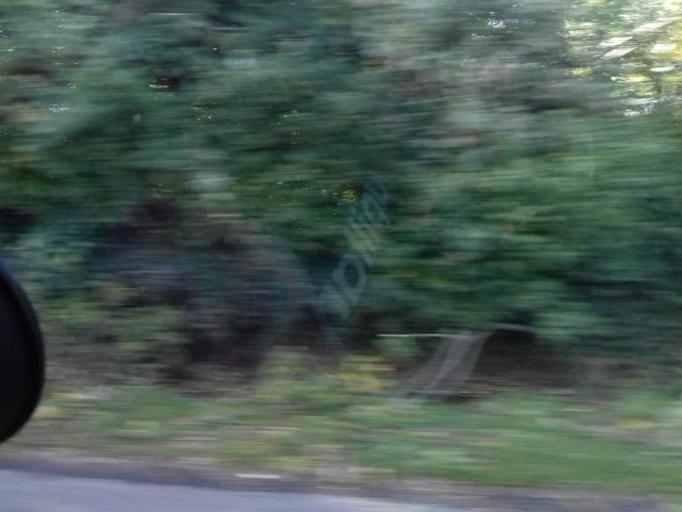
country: IE
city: Kentstown
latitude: 53.6354
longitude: -6.4948
